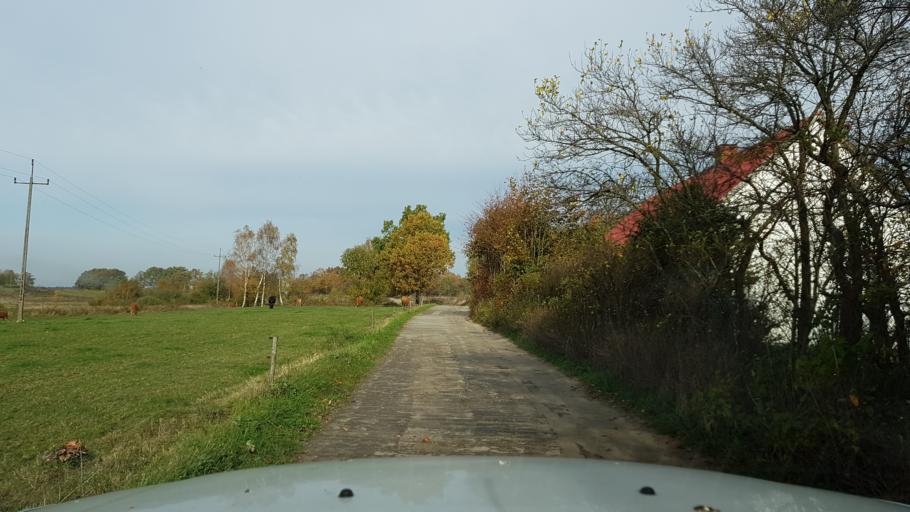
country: PL
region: West Pomeranian Voivodeship
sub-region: Powiat swidwinski
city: Polczyn-Zdroj
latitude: 53.7470
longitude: 16.0359
